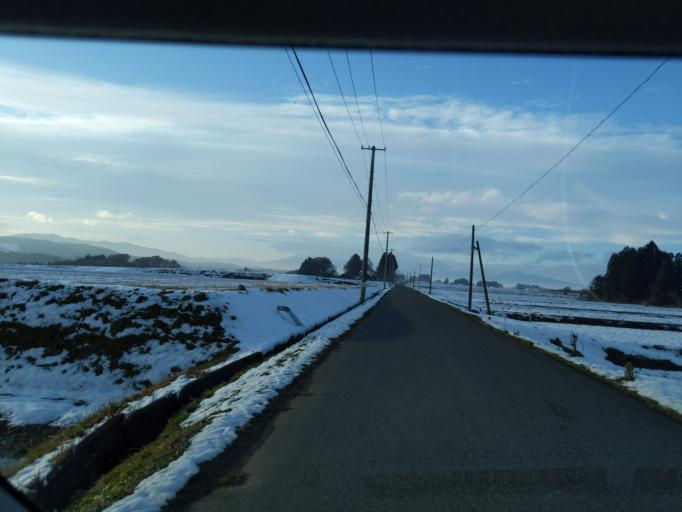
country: JP
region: Iwate
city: Mizusawa
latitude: 39.0480
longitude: 141.1063
